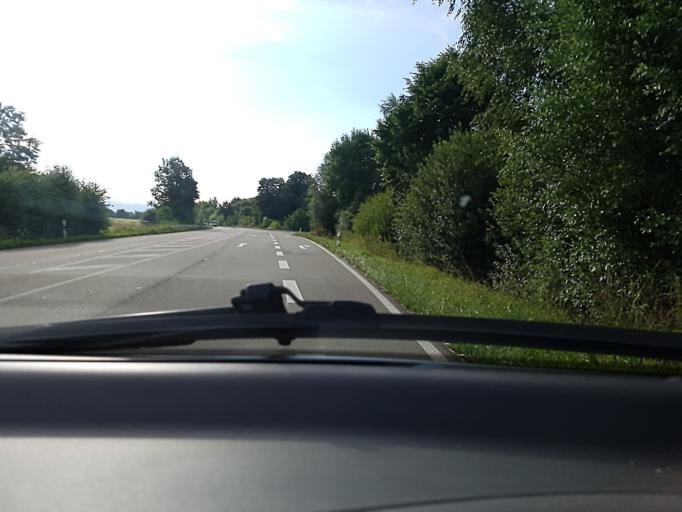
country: DE
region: Baden-Wuerttemberg
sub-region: Freiburg Region
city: Willstatt
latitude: 48.5336
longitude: 7.8763
